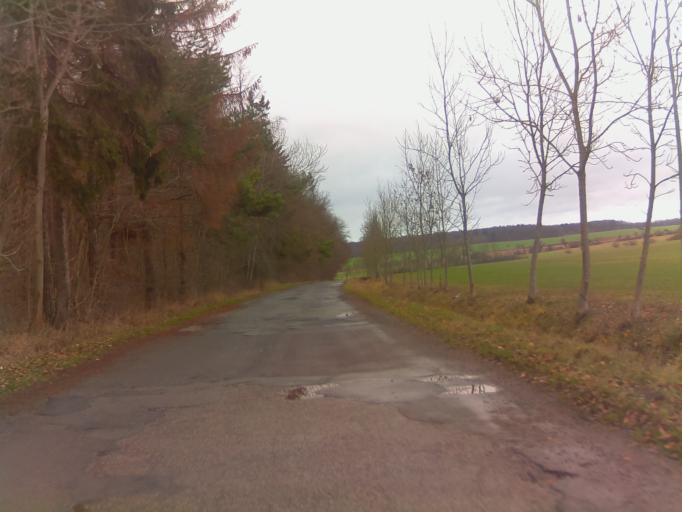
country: DE
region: Thuringia
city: Nauendorf
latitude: 50.9046
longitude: 11.1914
